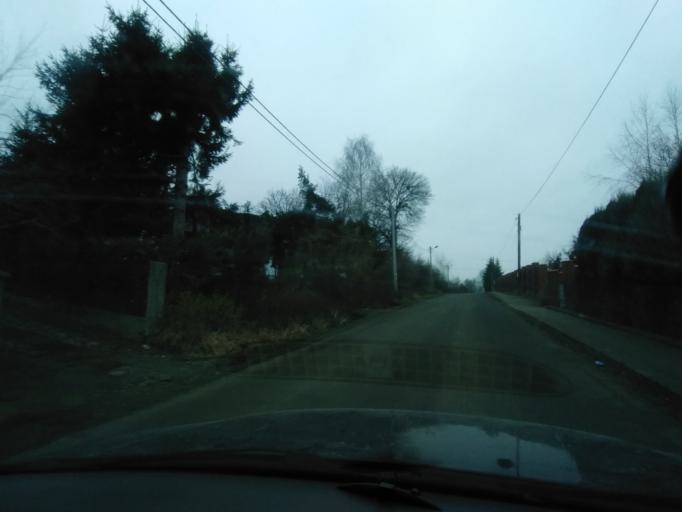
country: PL
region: Subcarpathian Voivodeship
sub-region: Powiat jaroslawski
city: Pruchnik
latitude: 49.9089
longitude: 22.5208
